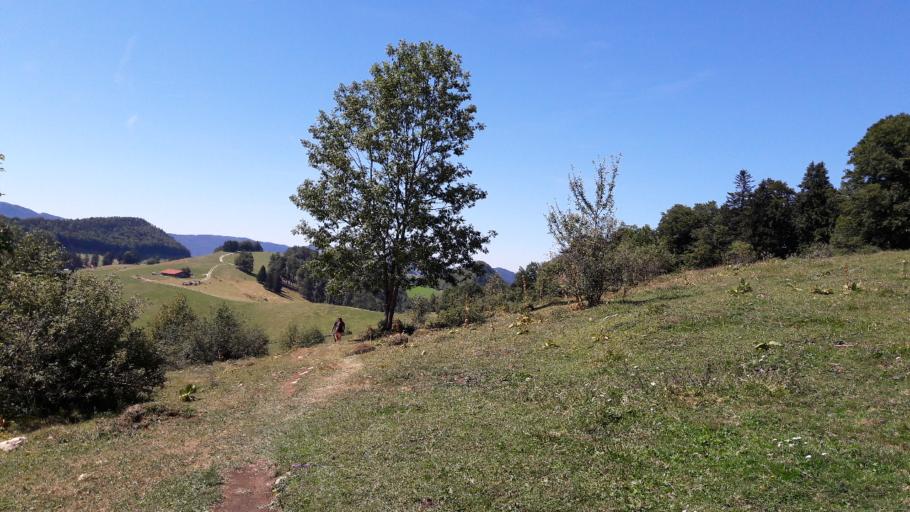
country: CH
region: Solothurn
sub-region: Bezirk Thal
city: Welschenrohr
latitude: 47.3153
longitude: 7.5707
